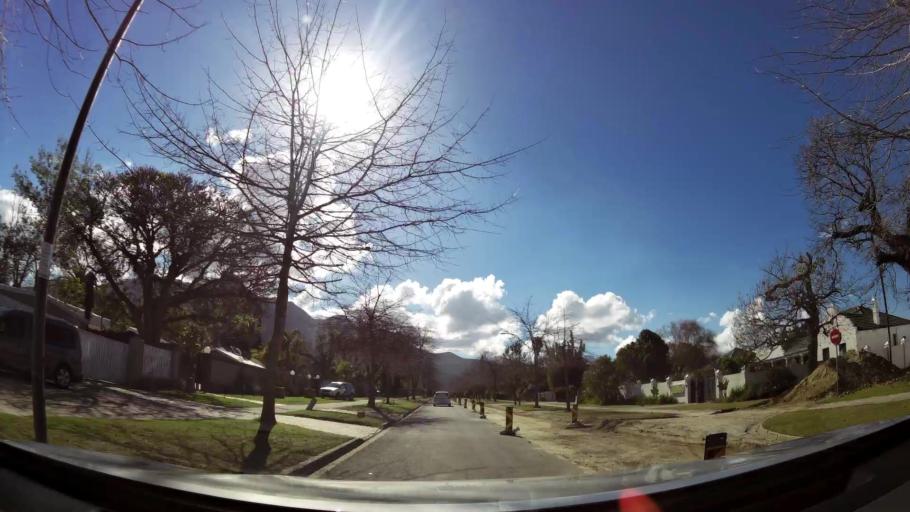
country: ZA
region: Western Cape
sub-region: Eden District Municipality
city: George
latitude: -33.9525
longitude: 22.4605
